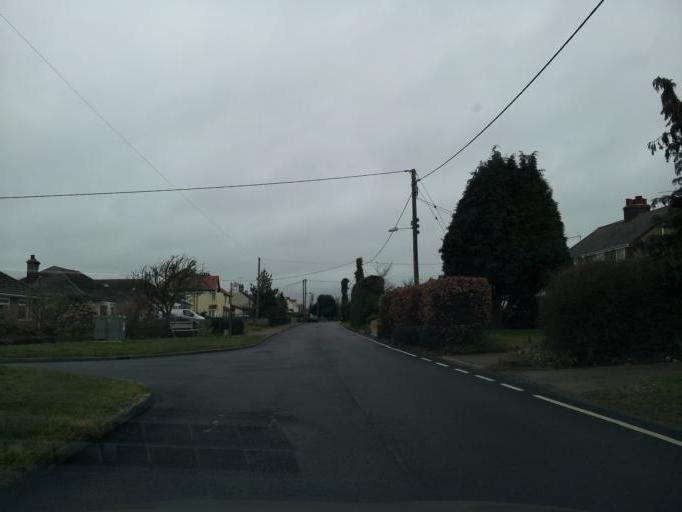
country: GB
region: England
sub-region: Essex
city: Dovercourt
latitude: 51.9243
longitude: 1.2298
